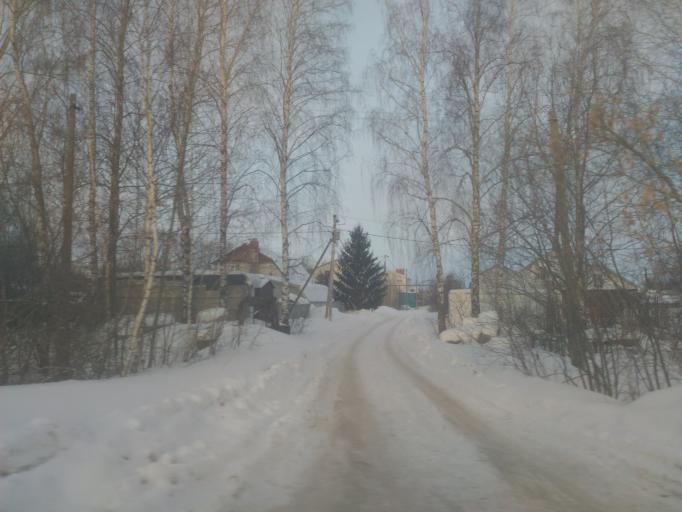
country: RU
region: Ulyanovsk
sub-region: Ulyanovskiy Rayon
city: Ulyanovsk
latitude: 54.3609
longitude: 48.3485
